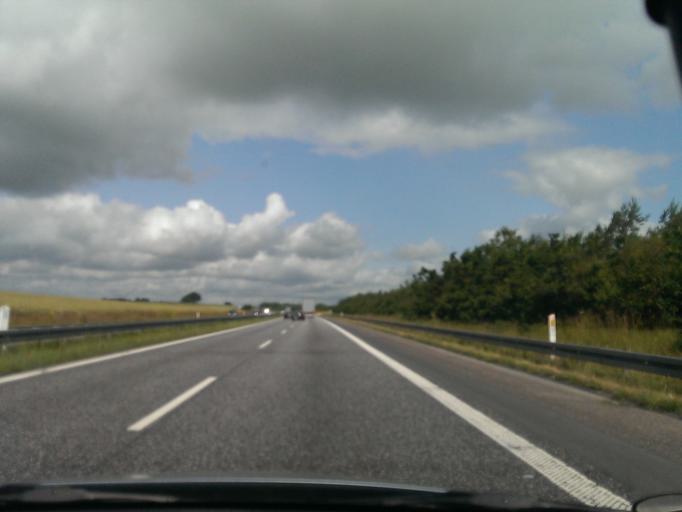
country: DK
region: Central Jutland
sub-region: Randers Kommune
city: Spentrup
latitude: 56.5201
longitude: 9.9564
